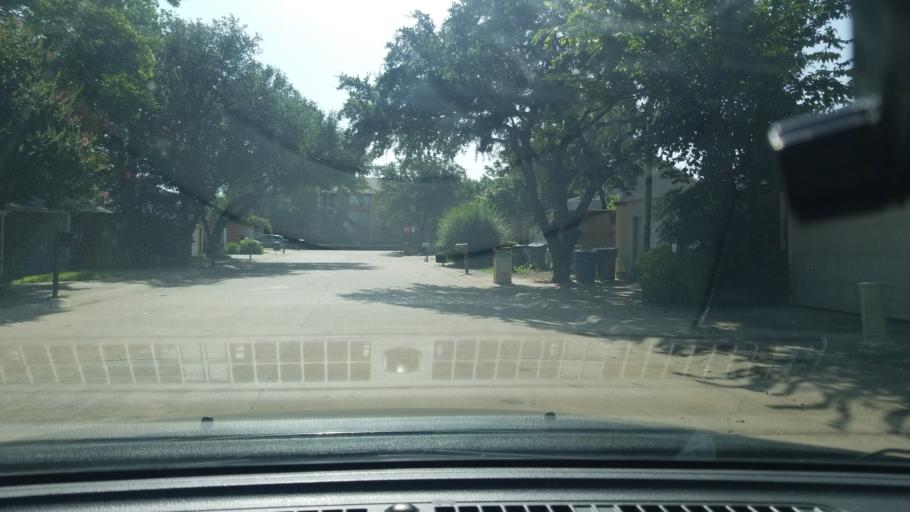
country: US
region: Texas
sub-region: Dallas County
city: Mesquite
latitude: 32.8107
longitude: -96.6905
